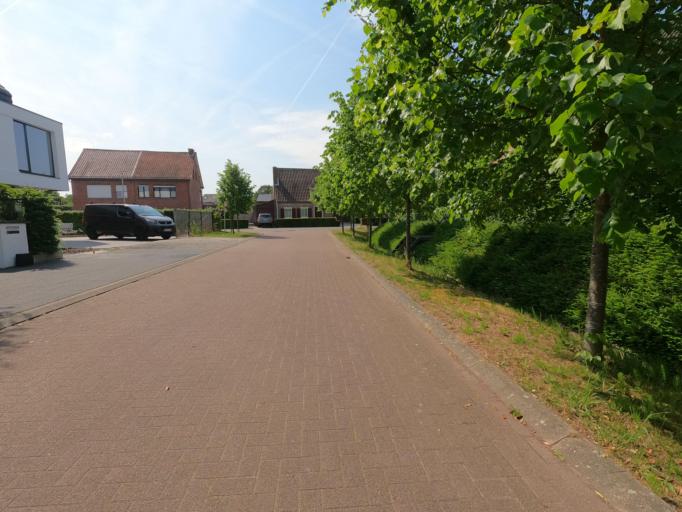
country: BE
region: Flanders
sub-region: Provincie Antwerpen
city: Nijlen
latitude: 51.1507
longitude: 4.6245
